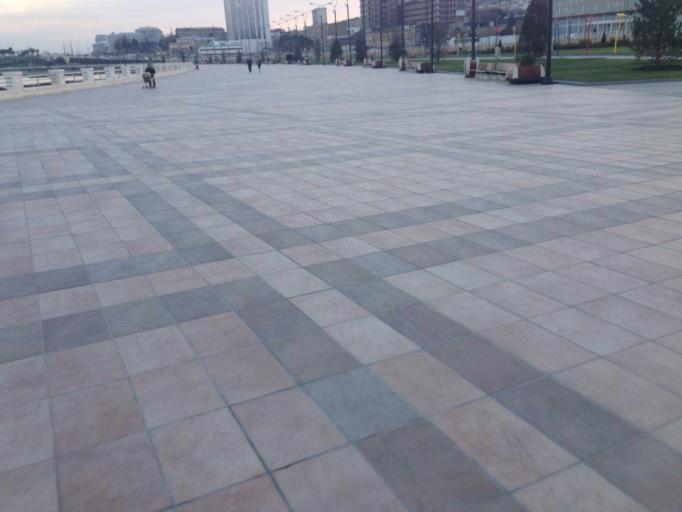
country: AZ
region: Baki
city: Badamdar
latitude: 40.3517
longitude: 49.8368
